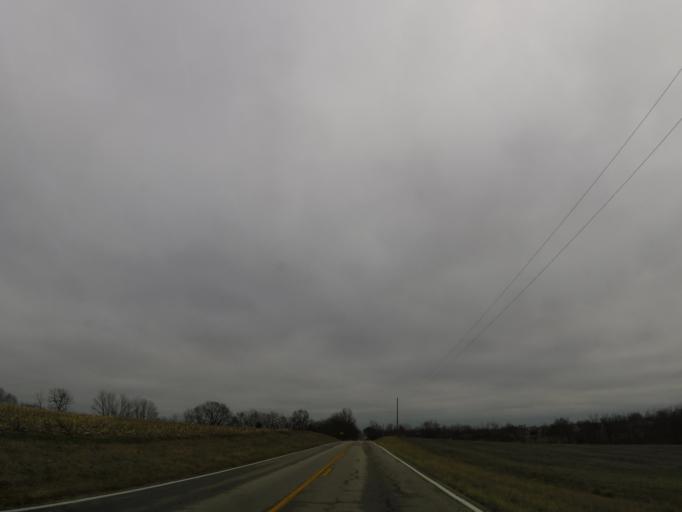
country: US
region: Kentucky
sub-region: Henry County
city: Eminence
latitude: 38.3935
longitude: -85.1614
